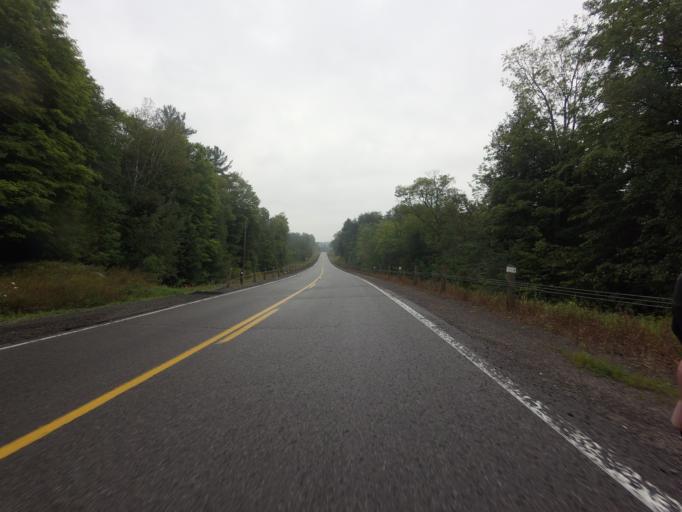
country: CA
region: Ontario
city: Carleton Place
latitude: 45.1096
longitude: -76.3741
